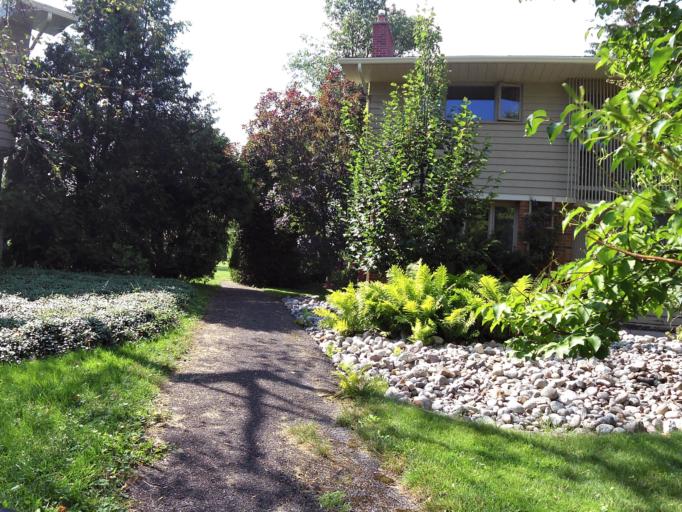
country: CA
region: Ontario
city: Bells Corners
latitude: 45.3336
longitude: -75.9115
